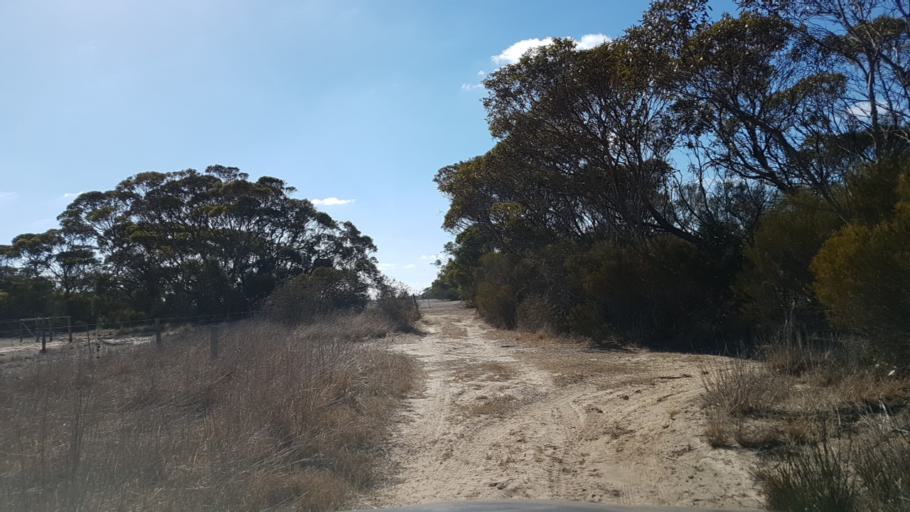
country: AU
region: South Australia
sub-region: Alexandrina
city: Strathalbyn
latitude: -35.3765
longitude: 138.8340
